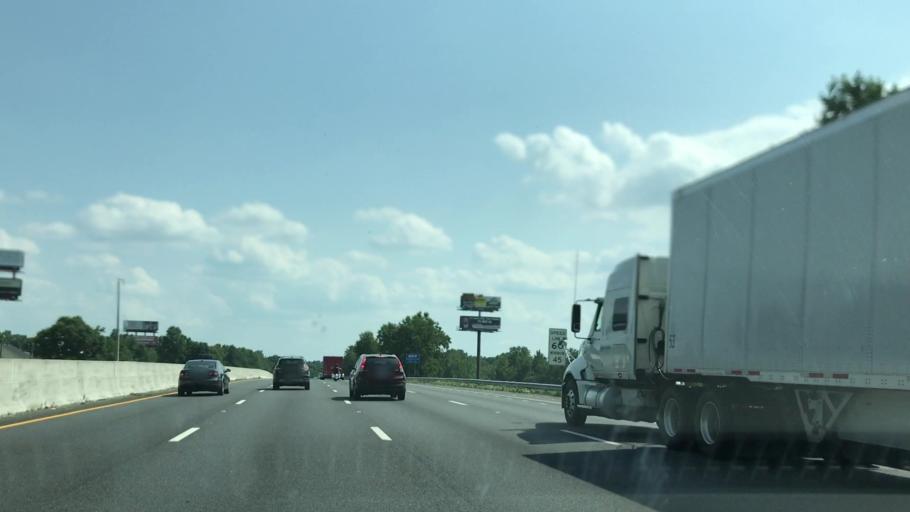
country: US
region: South Carolina
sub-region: York County
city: Fort Mill
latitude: 35.0108
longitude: -80.9705
